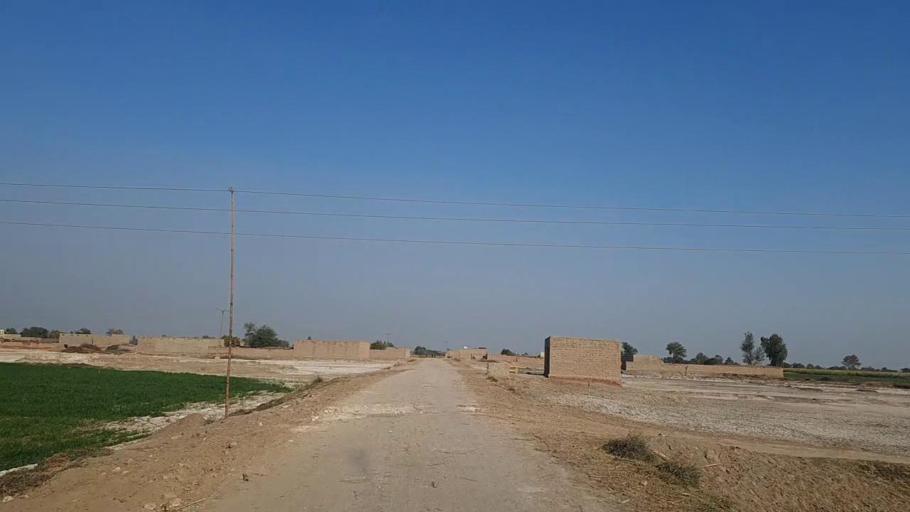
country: PK
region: Sindh
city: Daur
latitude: 26.3170
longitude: 68.1677
